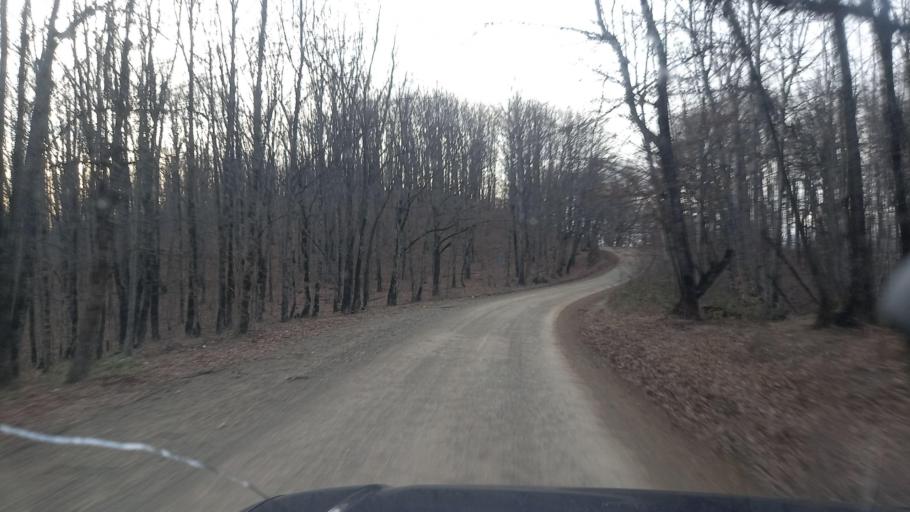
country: RU
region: Krasnodarskiy
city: Goryachiy Klyuch
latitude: 44.3709
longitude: 39.2166
